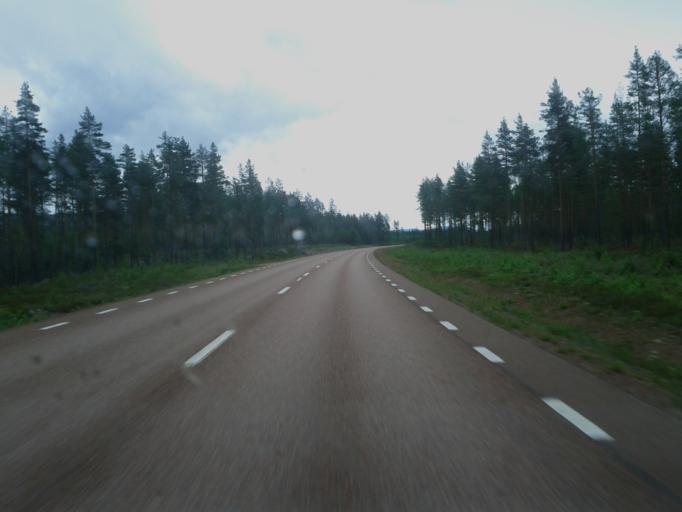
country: SE
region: Dalarna
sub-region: Alvdalens Kommun
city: AElvdalen
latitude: 61.2785
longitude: 13.8603
